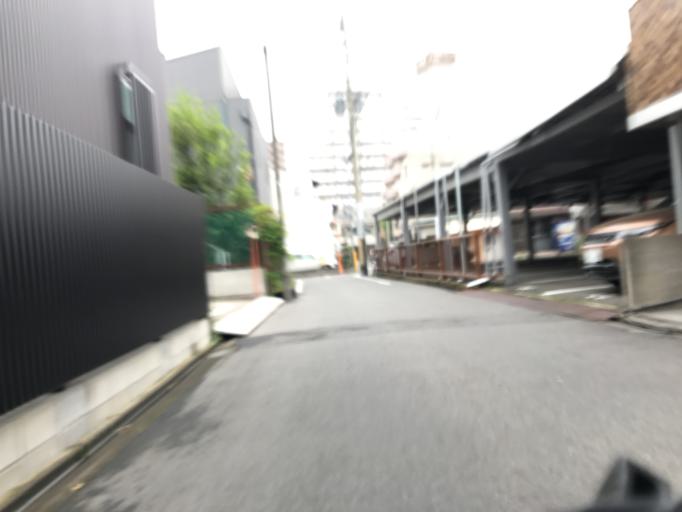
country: JP
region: Aichi
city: Nagoya-shi
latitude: 35.1739
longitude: 136.8917
